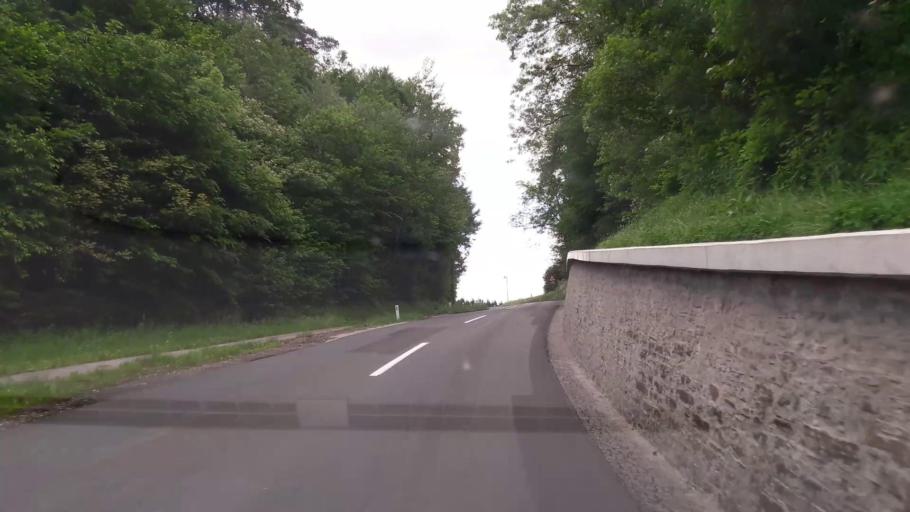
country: AT
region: Styria
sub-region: Politischer Bezirk Hartberg-Fuerstenfeld
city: Soechau
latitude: 47.0578
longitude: 16.0094
